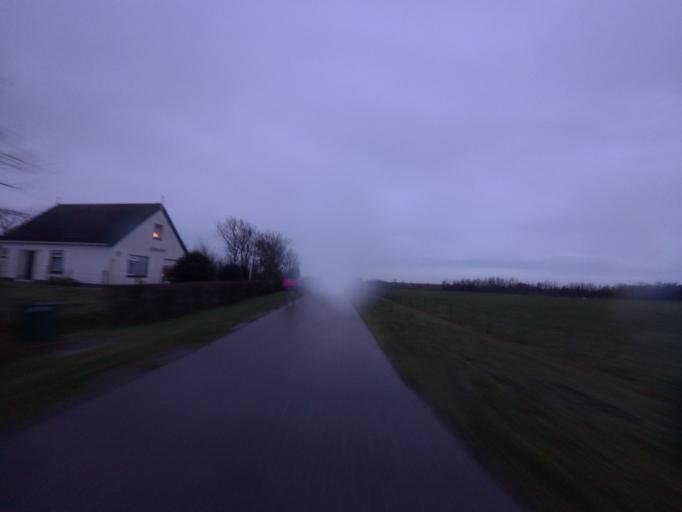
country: NL
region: North Holland
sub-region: Gemeente Texel
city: Den Burg
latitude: 53.0668
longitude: 4.7987
